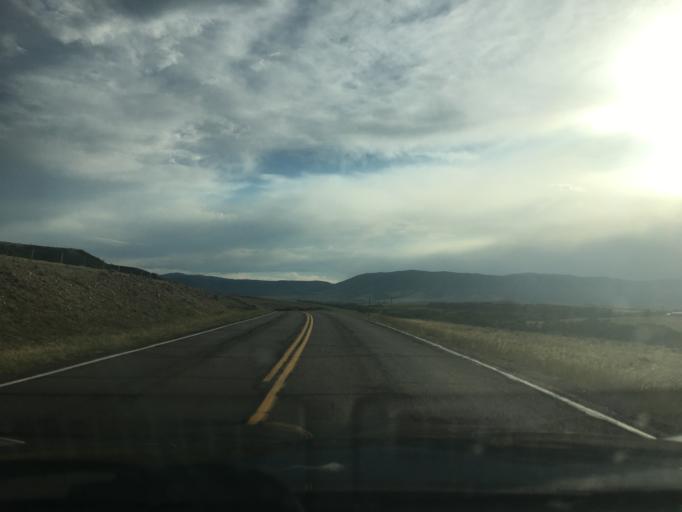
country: US
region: Wyoming
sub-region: Albany County
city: Laramie
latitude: 41.2842
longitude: -106.0547
